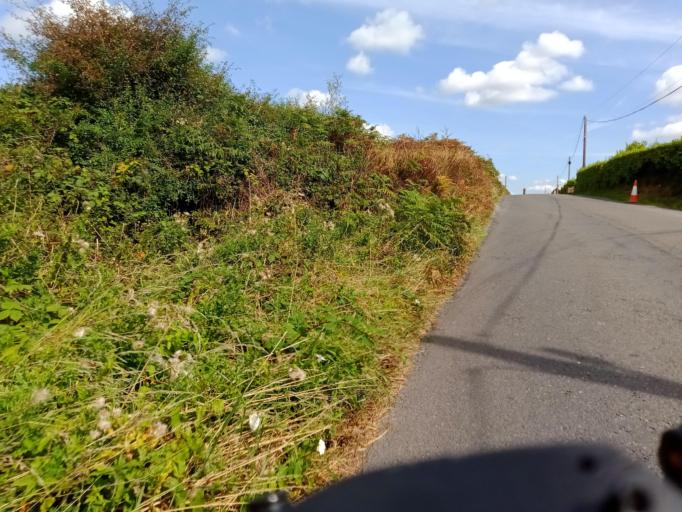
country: IE
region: Munster
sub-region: Waterford
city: Dungarvan
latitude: 52.1184
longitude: -7.4911
